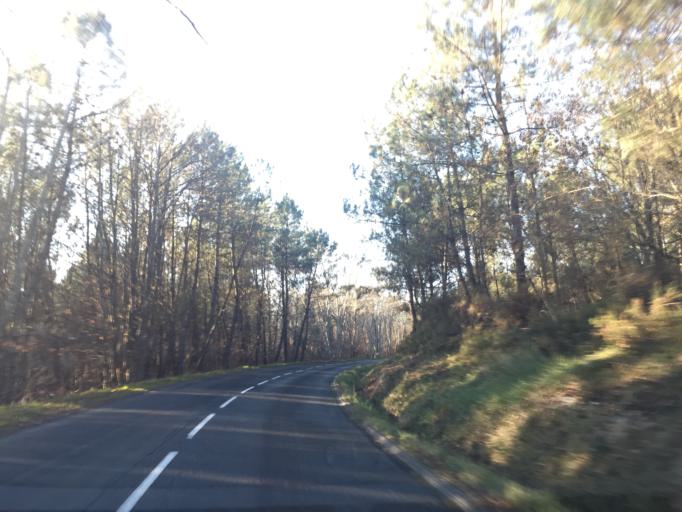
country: FR
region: Aquitaine
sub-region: Departement de la Dordogne
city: Neuvic
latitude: 45.1546
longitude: 0.4182
